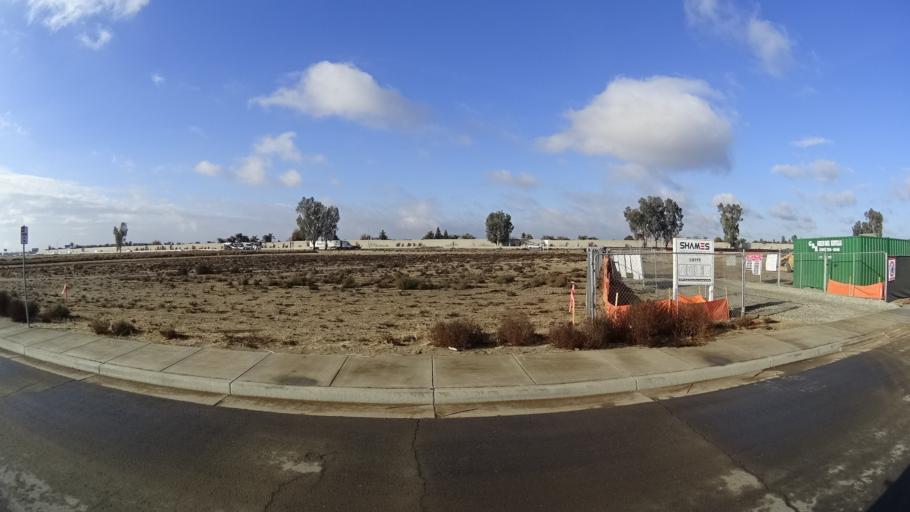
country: US
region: California
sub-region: Kern County
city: Greenfield
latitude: 35.2902
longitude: -119.0264
